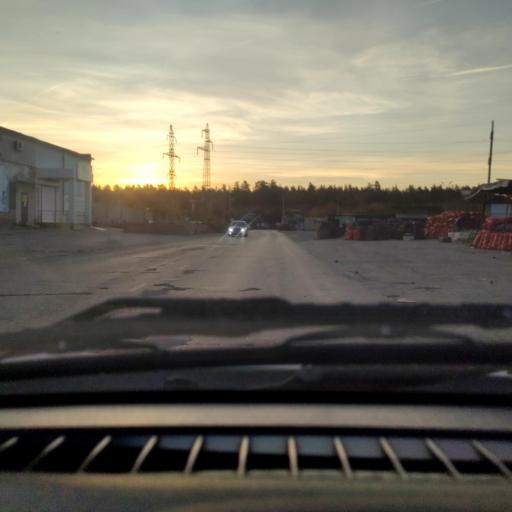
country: RU
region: Samara
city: Zhigulevsk
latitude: 53.5191
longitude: 49.4803
